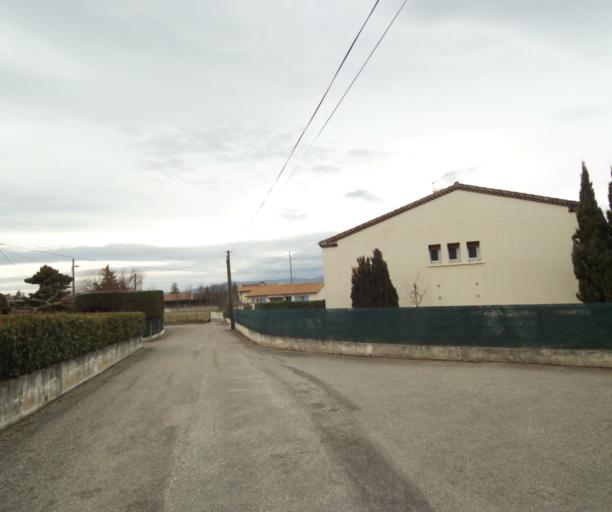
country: FR
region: Rhone-Alpes
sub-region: Departement de l'Ardeche
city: Davezieux
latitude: 45.2572
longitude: 4.7019
